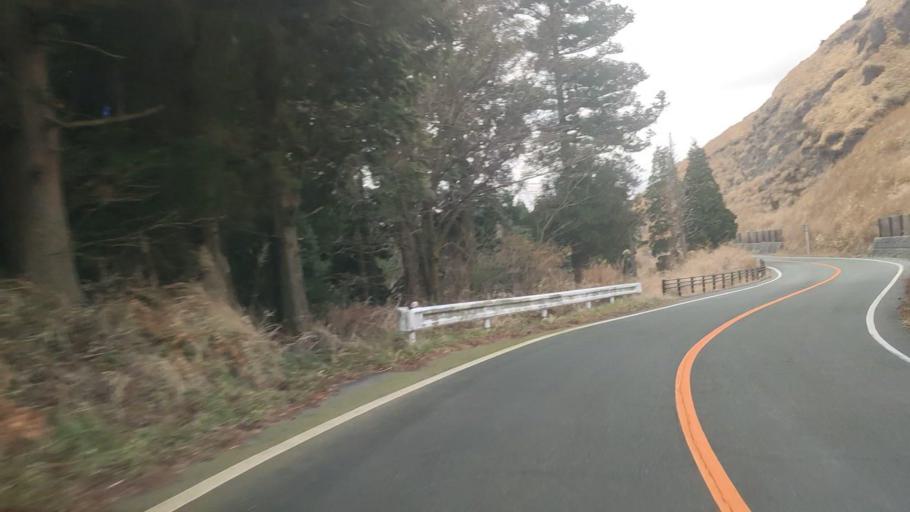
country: JP
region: Kumamoto
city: Aso
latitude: 32.9085
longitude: 131.1411
